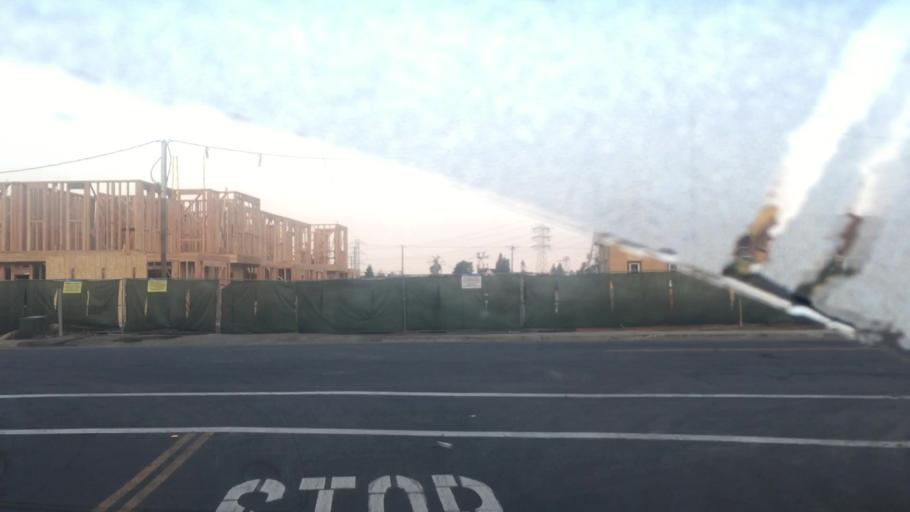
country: US
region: California
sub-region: Napa County
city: American Canyon
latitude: 38.1665
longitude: -122.2500
